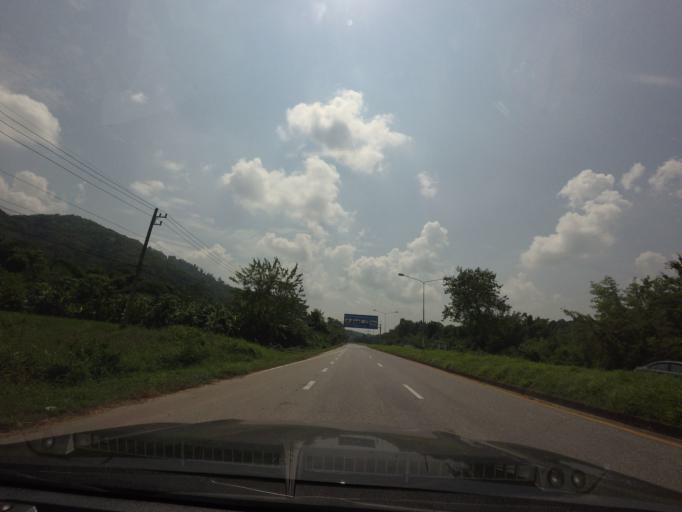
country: TH
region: Uttaradit
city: Lap Lae
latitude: 17.7949
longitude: 100.1164
